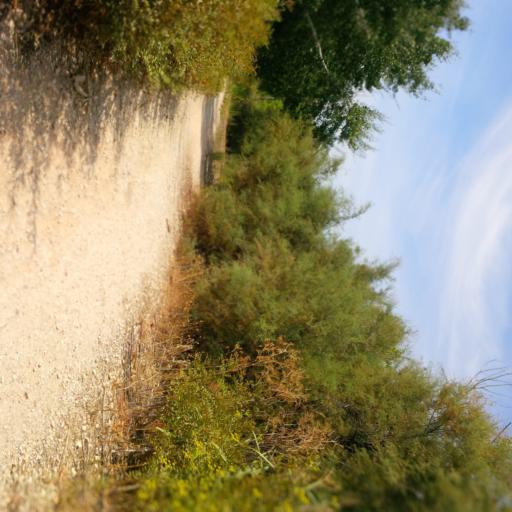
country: ES
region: Madrid
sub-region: Provincia de Madrid
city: Mejorada del Campo
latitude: 40.4121
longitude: -3.4923
